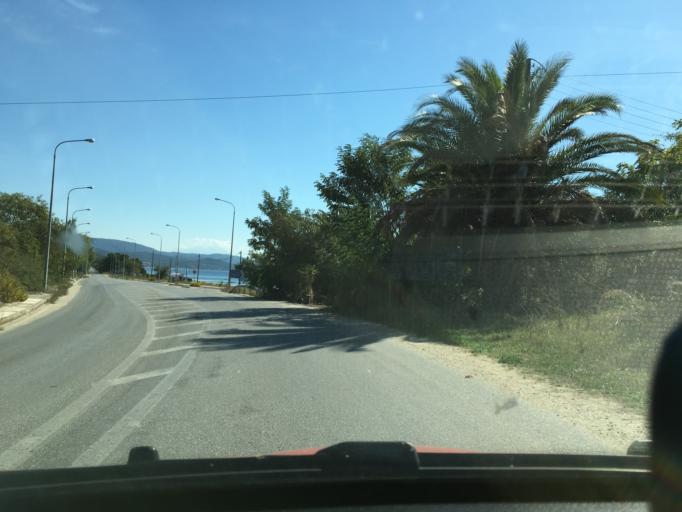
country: GR
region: Central Macedonia
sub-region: Nomos Chalkidikis
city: Nea Roda
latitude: 40.3657
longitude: 23.9179
